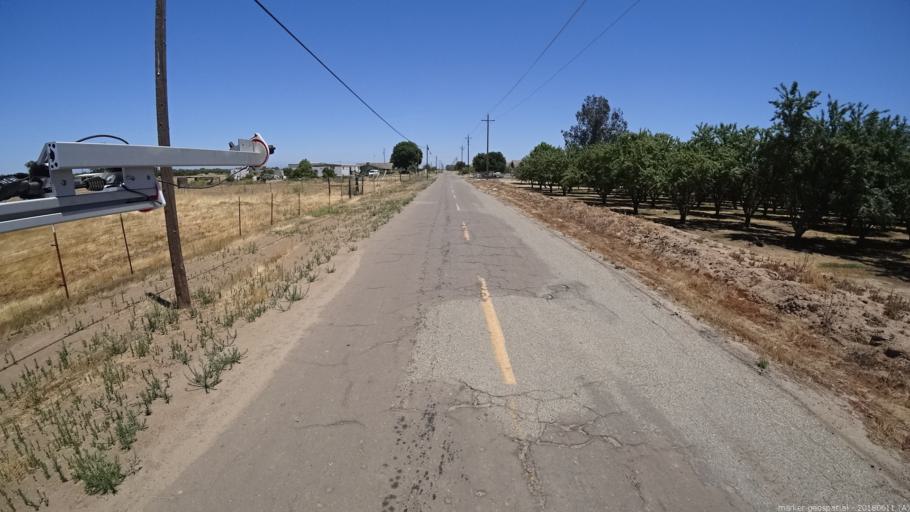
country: US
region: California
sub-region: Madera County
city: Fairmead
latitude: 37.0692
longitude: -120.2100
